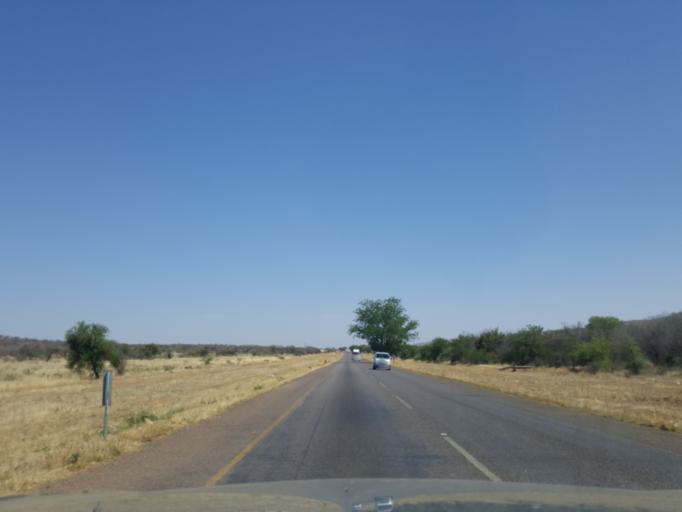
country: BW
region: South East
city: Lobatse
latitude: -25.1615
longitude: 25.6887
